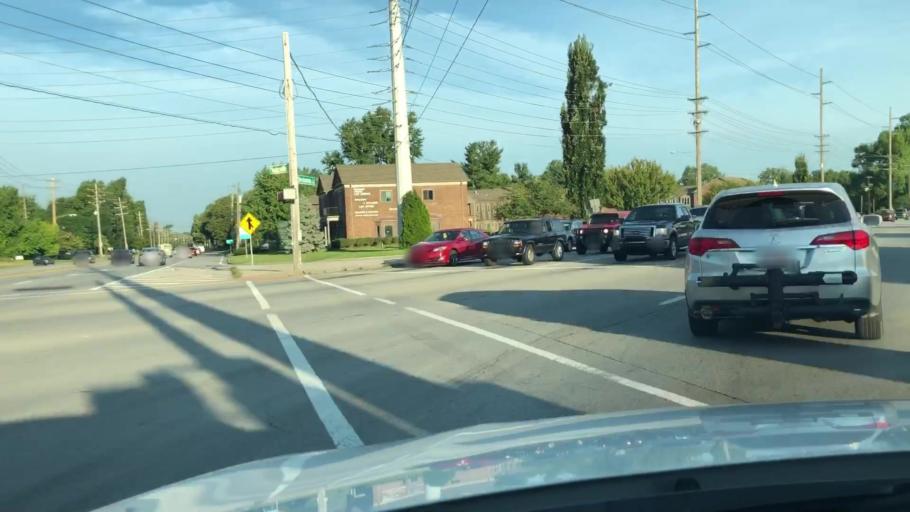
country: US
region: Kentucky
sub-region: Jefferson County
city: Saint Regis Park
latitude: 38.2203
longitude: -85.6305
